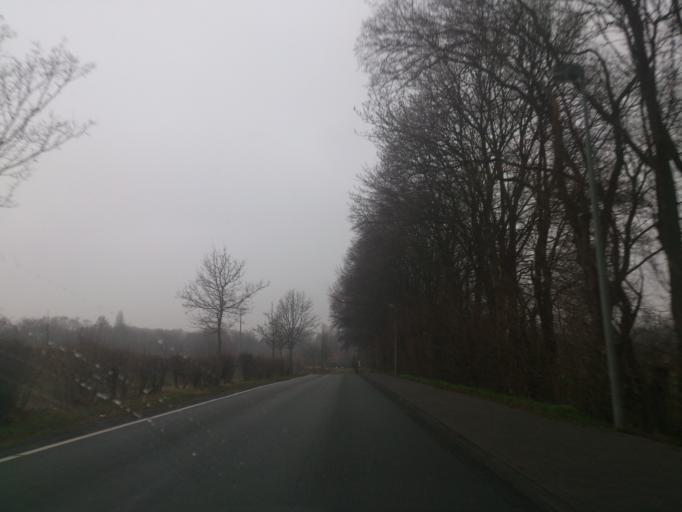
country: DE
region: North Rhine-Westphalia
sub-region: Regierungsbezirk Detmold
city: Paderborn
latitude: 51.7168
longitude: 8.7828
